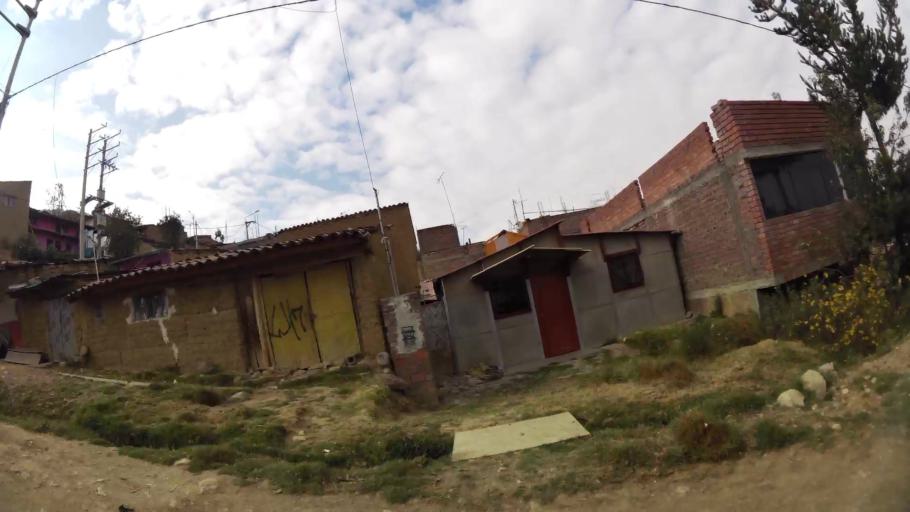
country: PE
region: Junin
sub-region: Provincia de Huancayo
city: Huancayo
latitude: -12.0527
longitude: -75.1858
